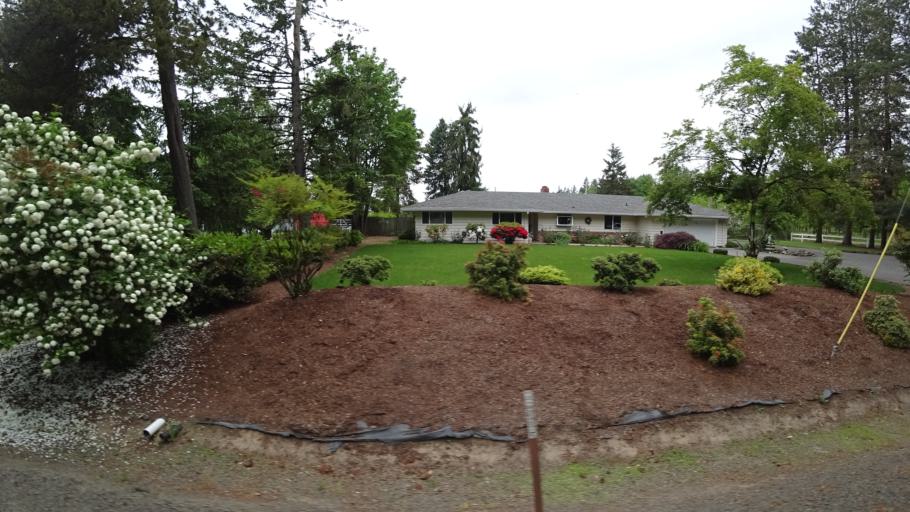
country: US
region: Oregon
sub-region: Washington County
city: Hillsboro
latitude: 45.4802
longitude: -122.9901
